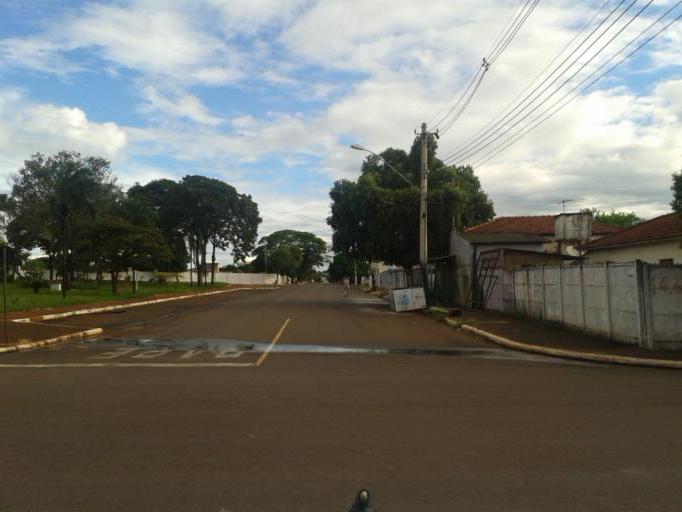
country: BR
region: Minas Gerais
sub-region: Ituiutaba
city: Ituiutaba
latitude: -18.9653
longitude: -49.4551
